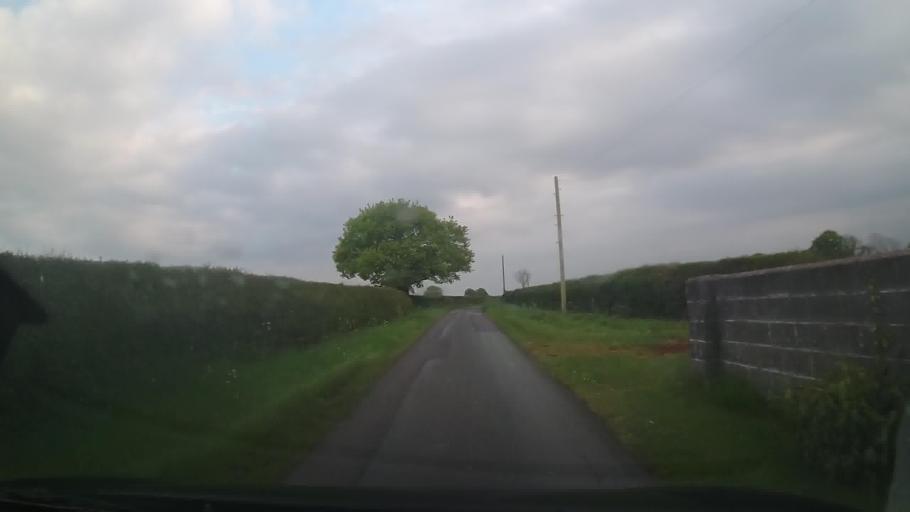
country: GB
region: England
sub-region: Shropshire
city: Ellesmere
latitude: 52.9367
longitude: -2.8609
